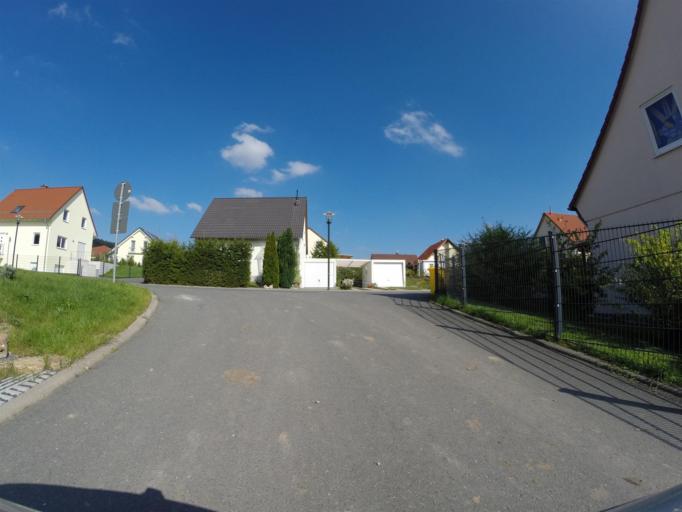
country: DE
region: Thuringia
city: Laasdorf
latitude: 50.8855
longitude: 11.6551
